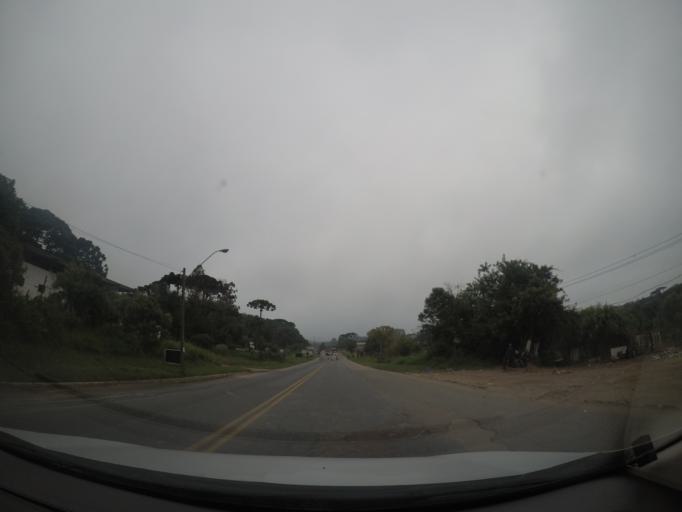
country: BR
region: Parana
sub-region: Almirante Tamandare
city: Almirante Tamandare
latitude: -25.3418
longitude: -49.2833
